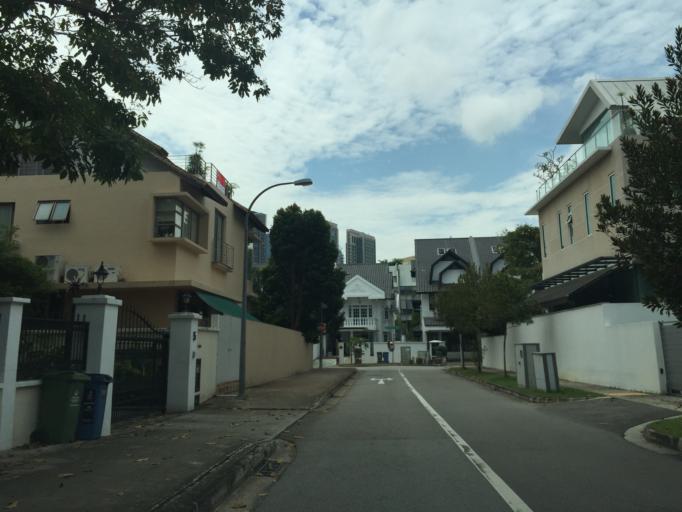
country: SG
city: Singapore
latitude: 1.3190
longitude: 103.8377
